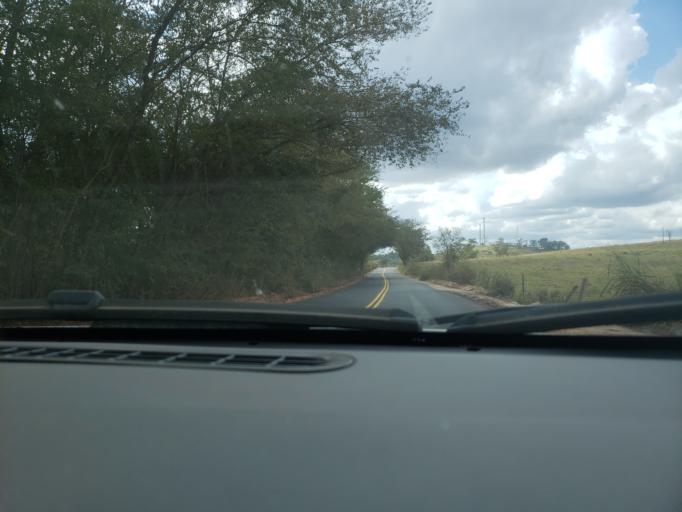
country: BR
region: Minas Gerais
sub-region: Campo Belo
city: Campo Belo
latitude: -20.9115
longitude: -45.2922
